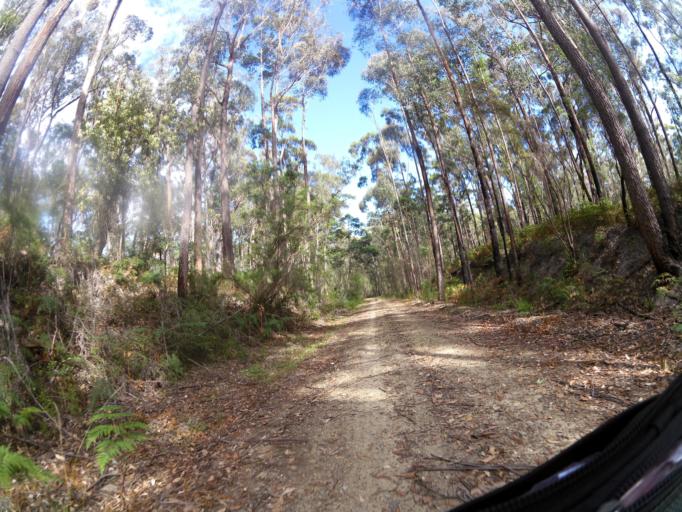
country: AU
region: Victoria
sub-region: East Gippsland
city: Lakes Entrance
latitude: -37.7509
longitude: 148.2092
